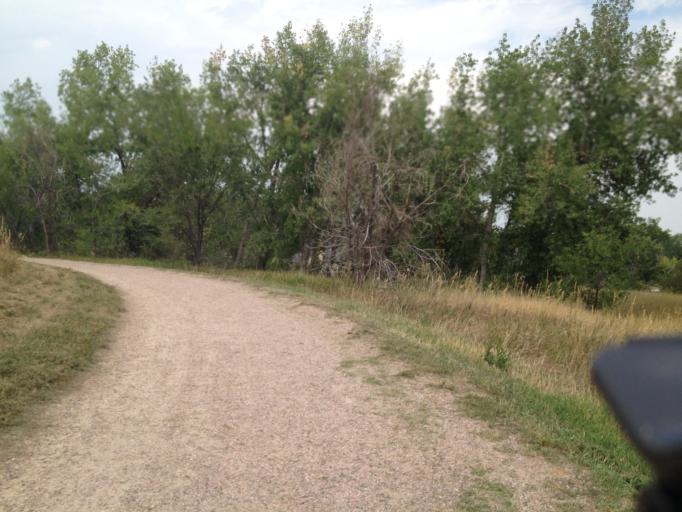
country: US
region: Colorado
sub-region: Boulder County
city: Louisville
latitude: 39.9854
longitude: -105.1473
